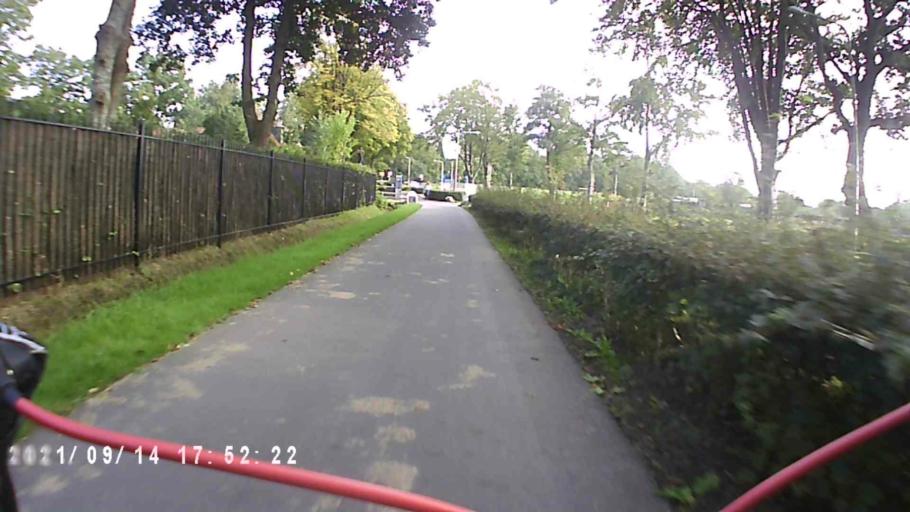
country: NL
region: Groningen
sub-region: Gemeente Haren
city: Haren
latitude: 53.1332
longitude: 6.6301
